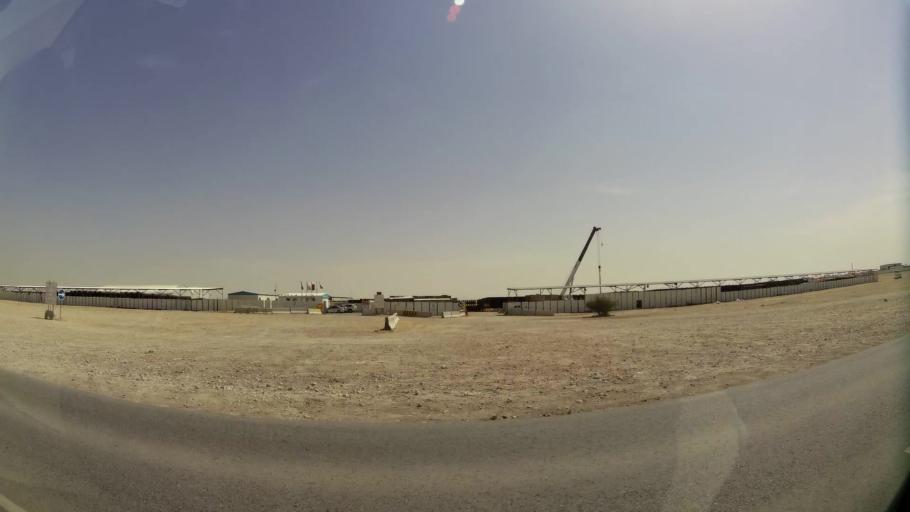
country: QA
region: Baladiyat ar Rayyan
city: Ar Rayyan
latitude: 25.2644
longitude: 51.3857
